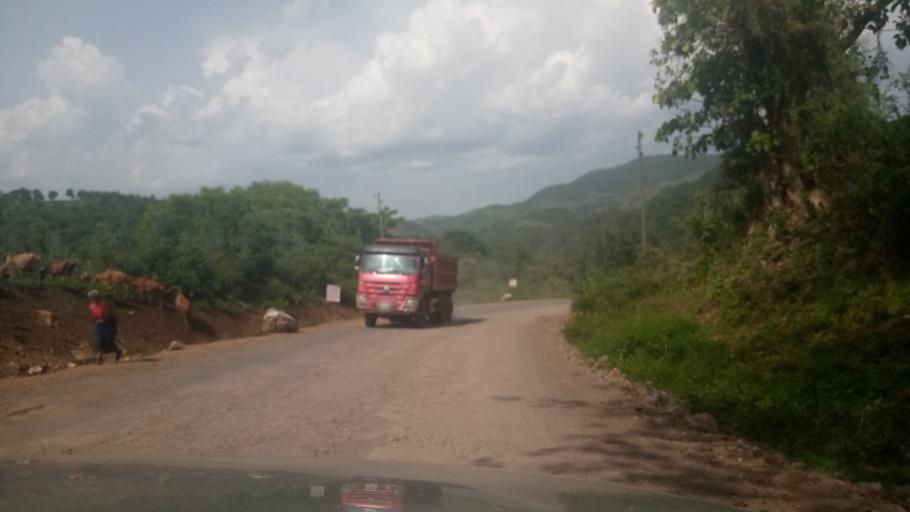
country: ET
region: Oromiya
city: Agaro
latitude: 8.0438
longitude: 36.4657
